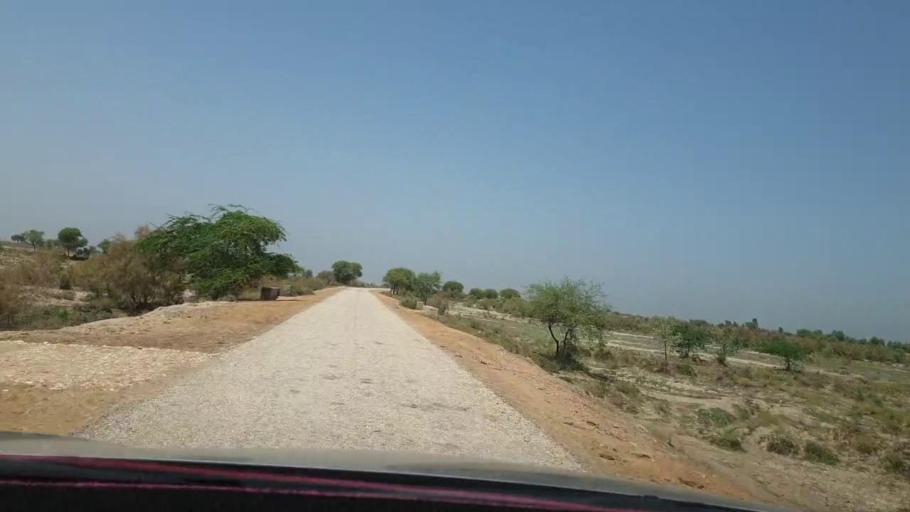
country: PK
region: Sindh
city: Warah
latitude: 27.5085
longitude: 67.7046
